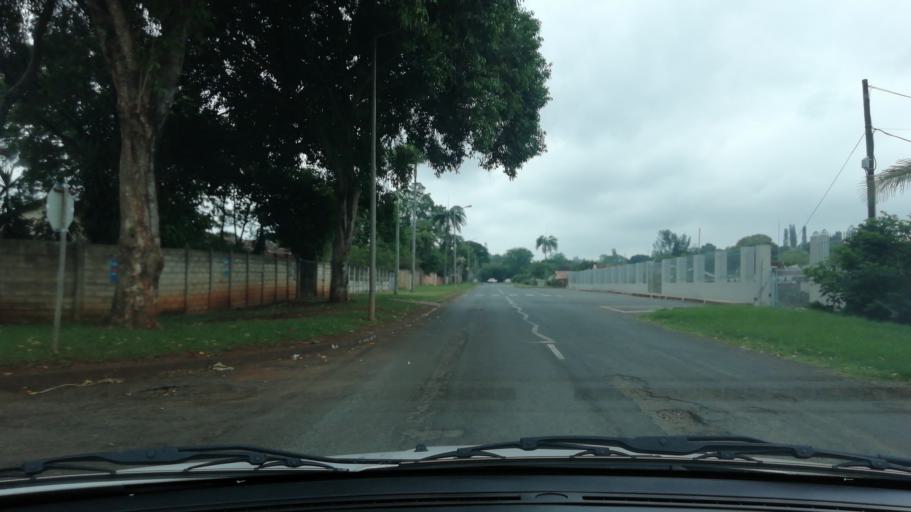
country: ZA
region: KwaZulu-Natal
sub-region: uThungulu District Municipality
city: Empangeni
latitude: -28.7614
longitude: 31.8990
